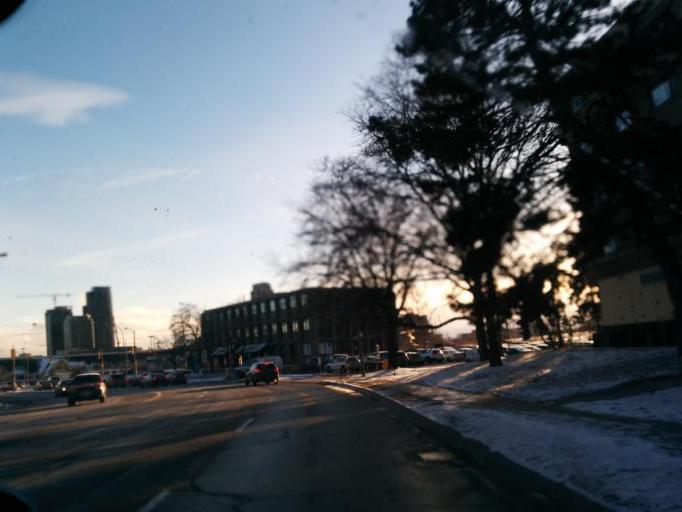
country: CA
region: Ontario
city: Etobicoke
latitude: 43.6475
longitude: -79.5603
